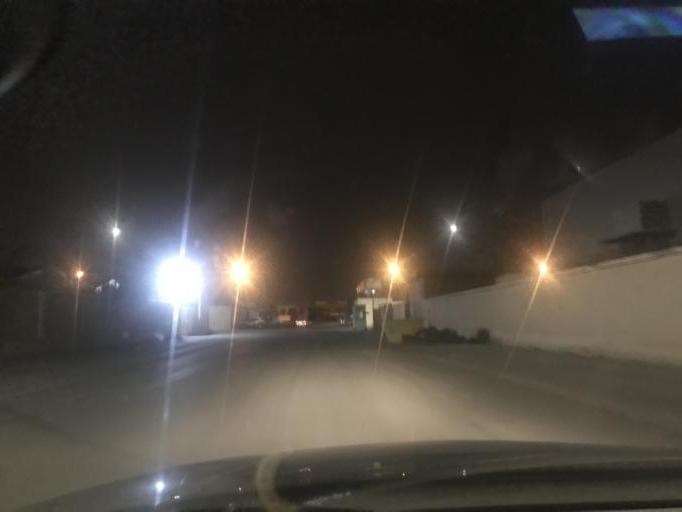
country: SA
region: Ar Riyad
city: Riyadh
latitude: 24.7250
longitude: 46.7829
